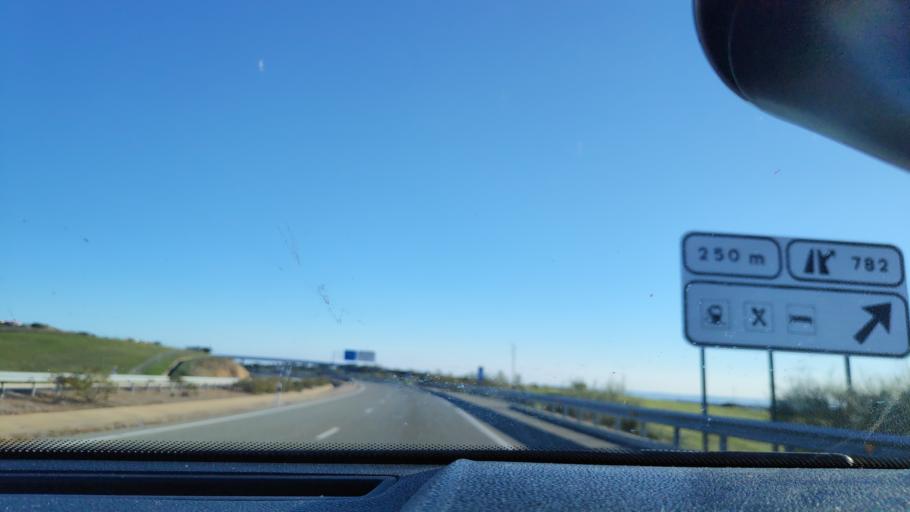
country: ES
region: Andalusia
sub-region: Provincia de Sevilla
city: El Ronquillo
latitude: 37.6311
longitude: -6.1480
